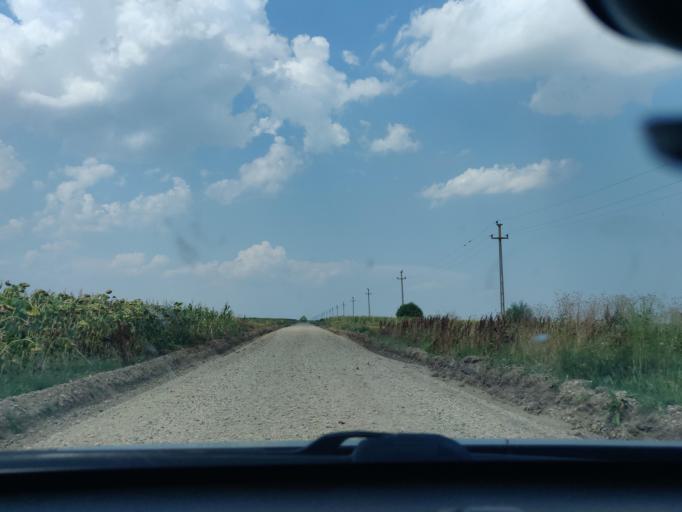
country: RO
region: Teleorman
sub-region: Comuna Sarbeni
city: Sarbeni
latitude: 44.4827
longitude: 25.3889
